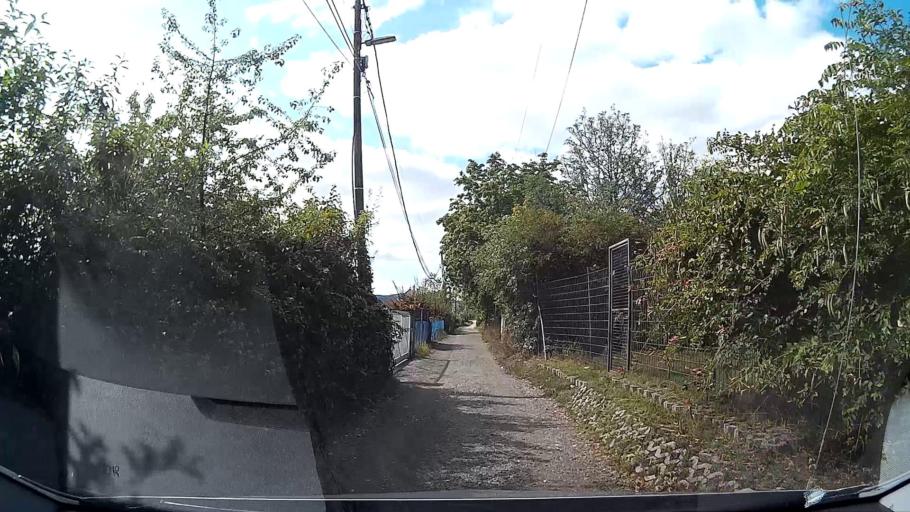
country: HU
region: Pest
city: Szentendre
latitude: 47.6934
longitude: 19.0664
